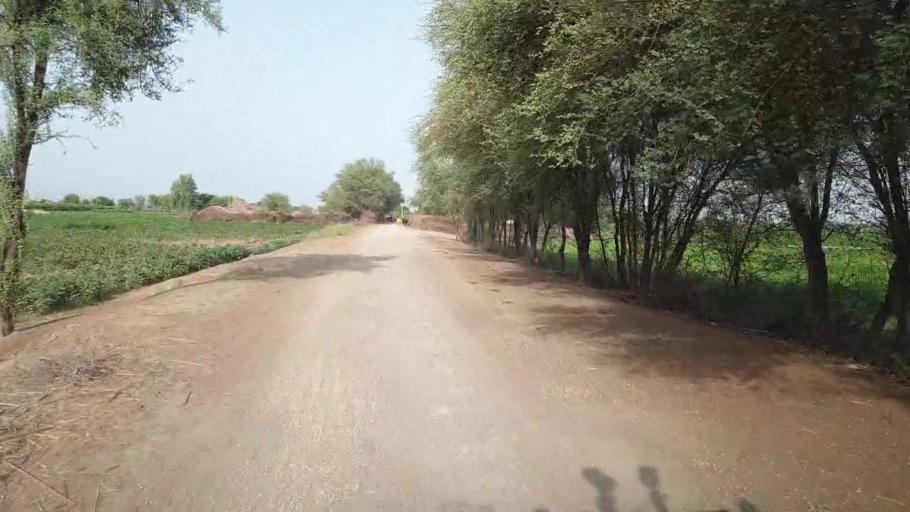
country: PK
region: Sindh
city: Daur
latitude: 26.3399
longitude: 68.2510
